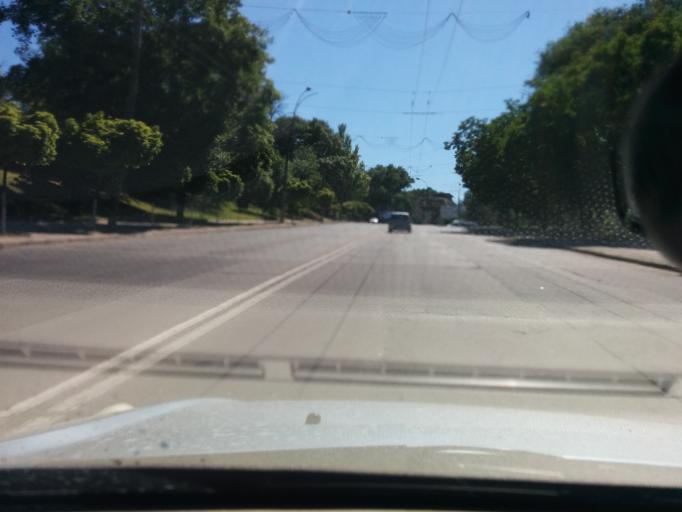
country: MD
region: Chisinau
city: Chisinau
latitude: 47.0391
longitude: 28.8562
